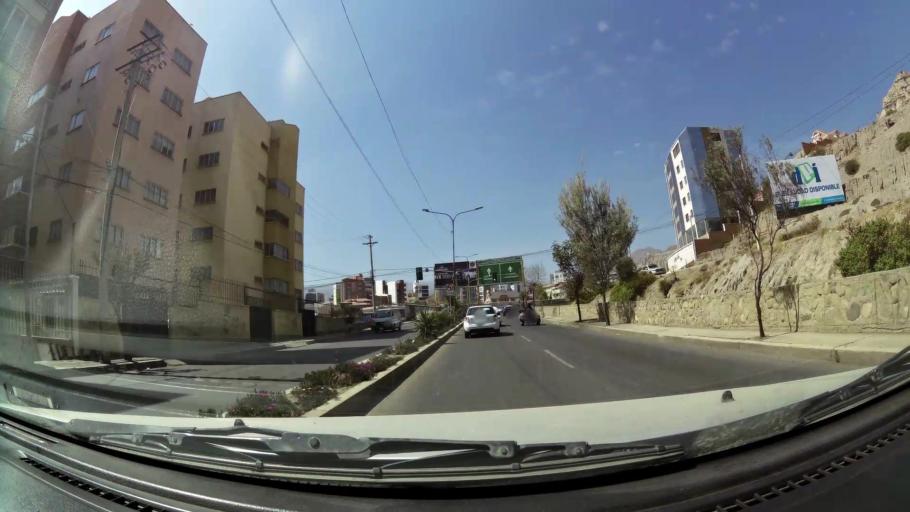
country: BO
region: La Paz
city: La Paz
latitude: -16.5453
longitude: -68.0828
